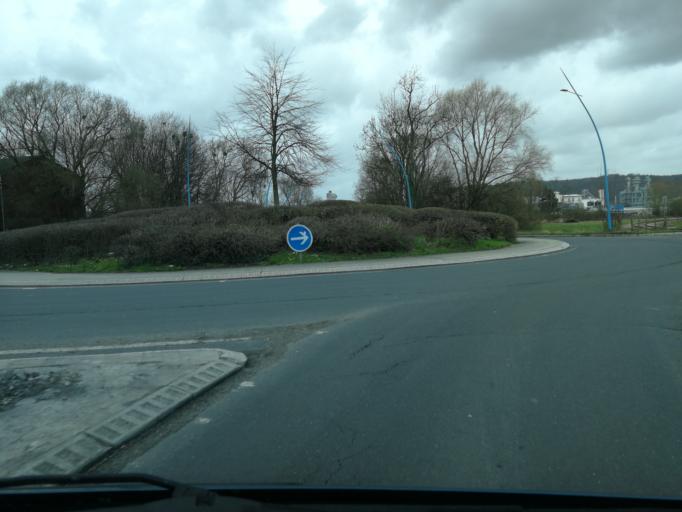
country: FR
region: Haute-Normandie
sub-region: Departement de l'Eure
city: Quillebeuf-sur-Seine
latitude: 49.4835
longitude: 0.5319
